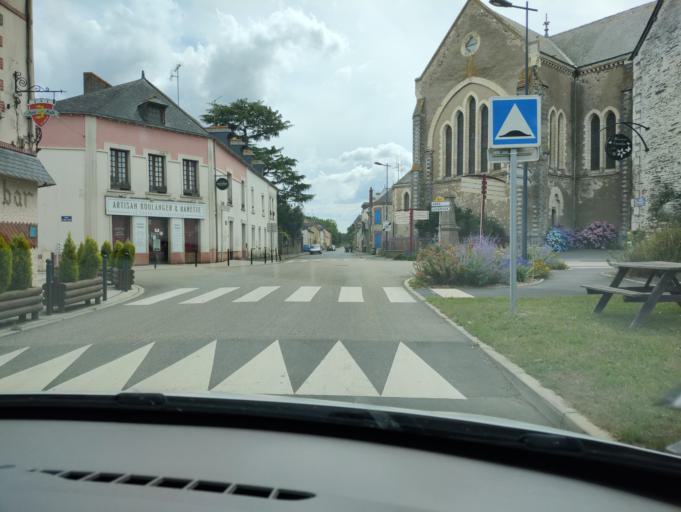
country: FR
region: Pays de la Loire
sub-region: Departement de la Loire-Atlantique
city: Saint-Vincent-des-Landes
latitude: 47.6198
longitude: -1.5375
